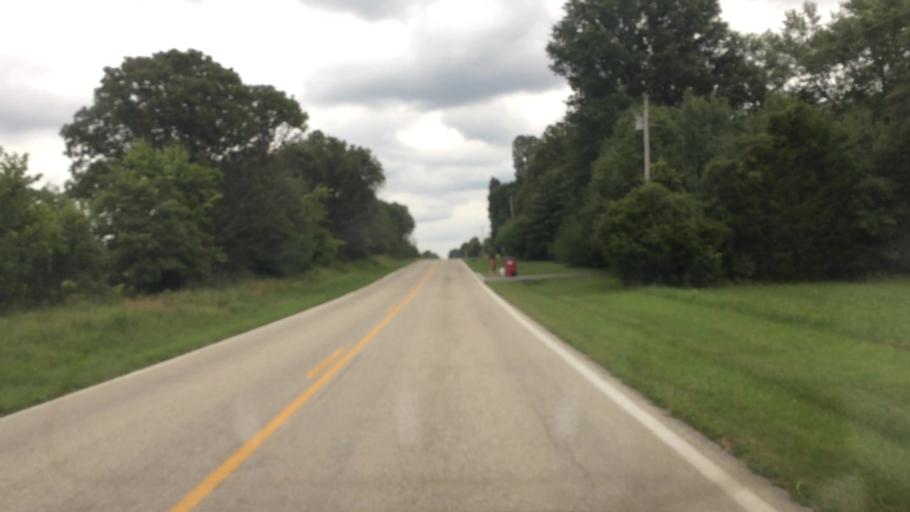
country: US
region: Missouri
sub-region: Greene County
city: Strafford
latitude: 37.3006
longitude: -93.1703
